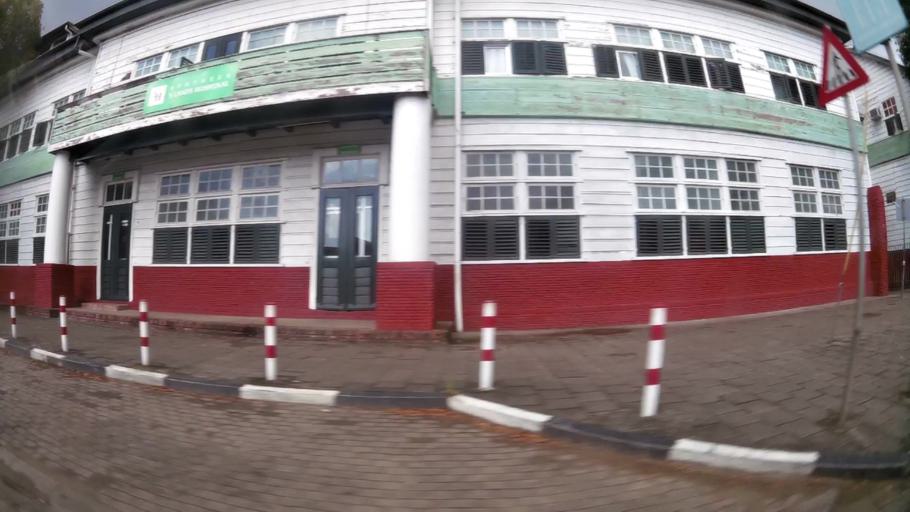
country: SR
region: Paramaribo
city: Paramaribo
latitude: 5.8299
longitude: -55.1570
